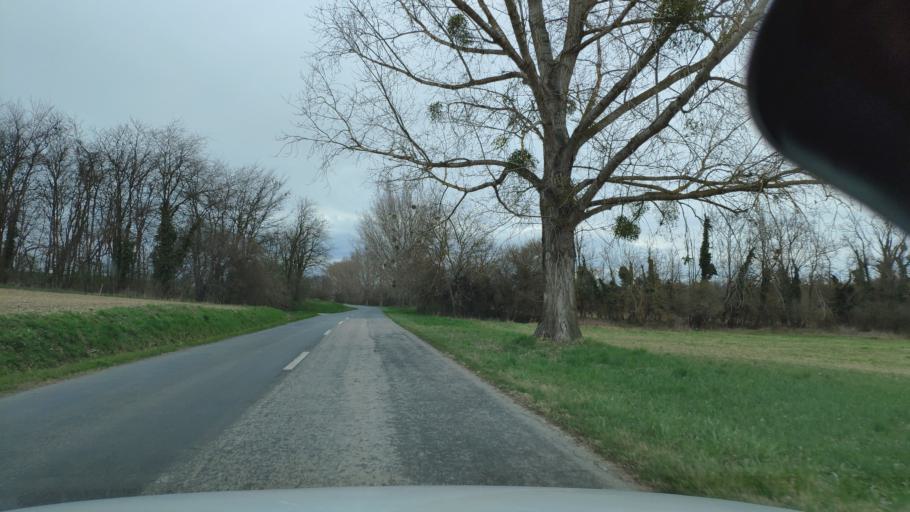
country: HU
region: Zala
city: Sarmellek
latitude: 46.6683
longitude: 17.1127
